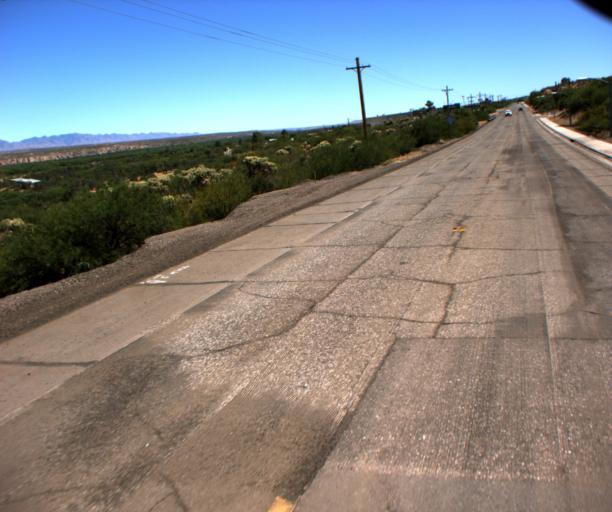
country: US
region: Arizona
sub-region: Pinal County
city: Mammoth
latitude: 32.7281
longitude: -110.6465
